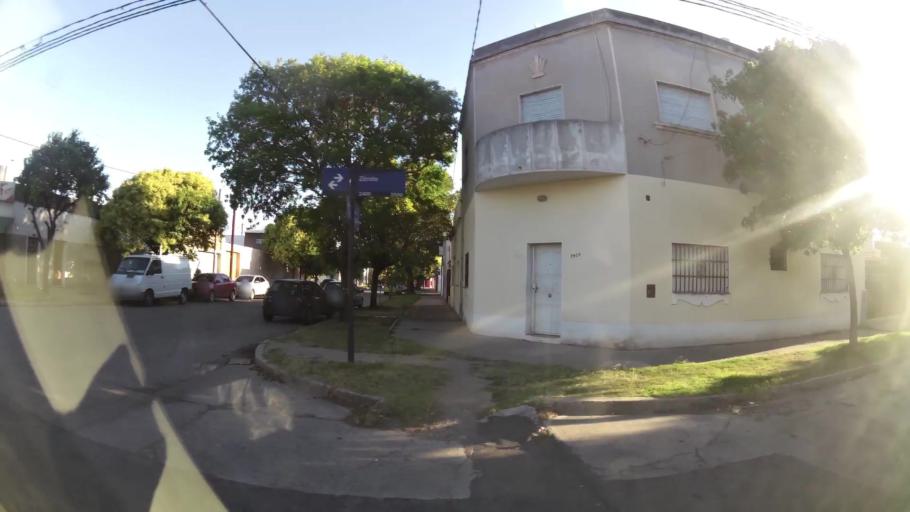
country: AR
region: Cordoba
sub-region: Departamento de Capital
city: Cordoba
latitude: -31.3759
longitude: -64.2057
